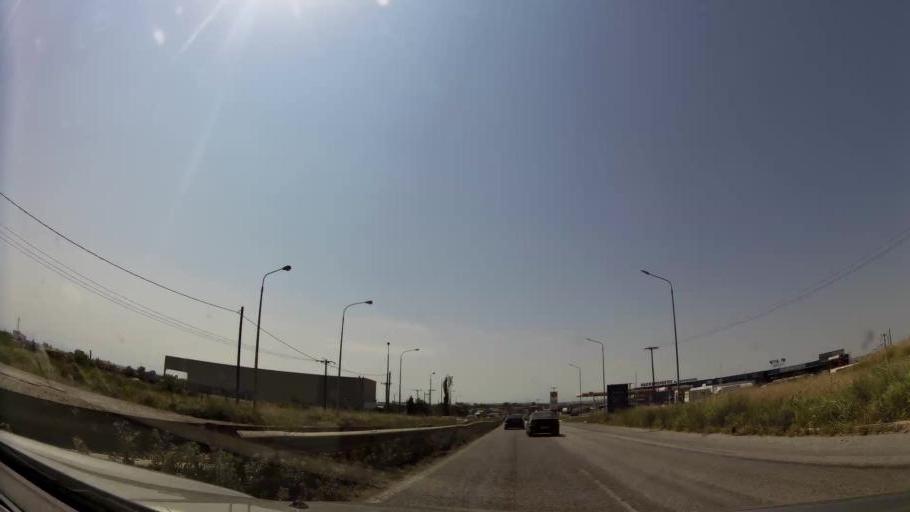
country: GR
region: Central Macedonia
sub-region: Nomos Thessalonikis
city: Sindos
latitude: 40.7045
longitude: 22.8119
